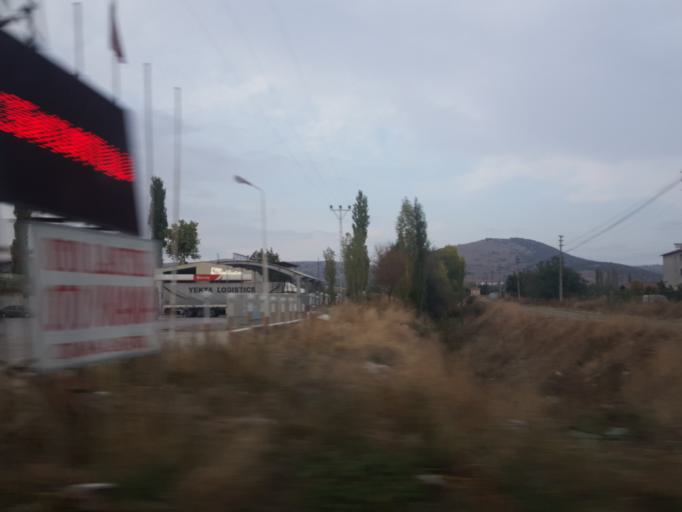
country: TR
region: Amasya
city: Gumushacikoy
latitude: 40.8856
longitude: 35.2090
